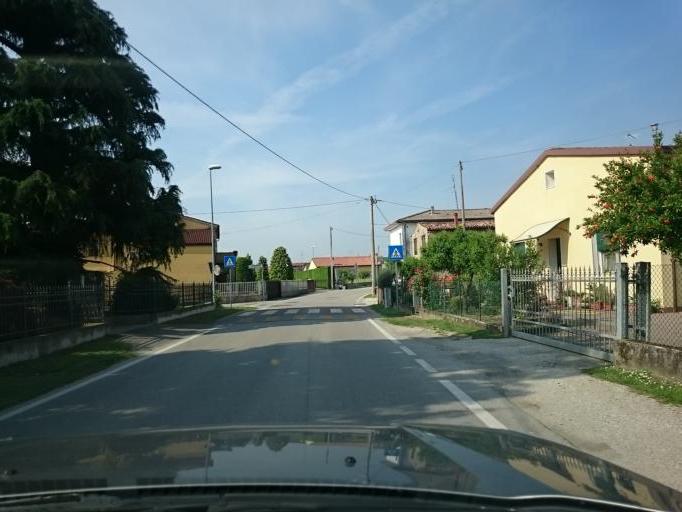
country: IT
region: Veneto
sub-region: Provincia di Padova
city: Ponte San Nicolo
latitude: 45.3603
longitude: 11.9172
